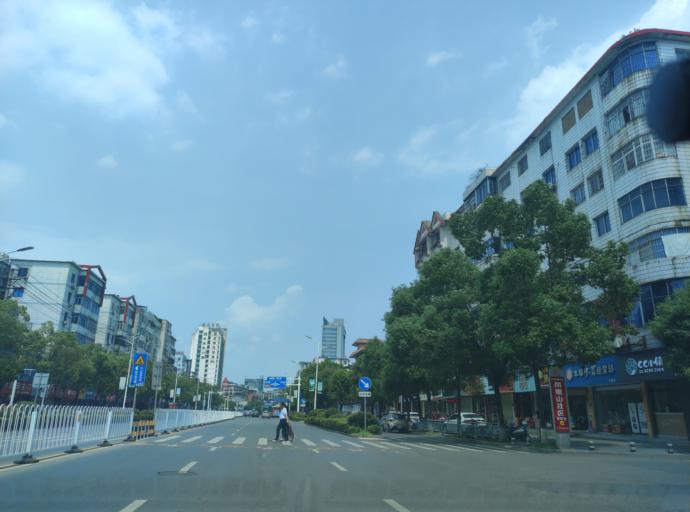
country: CN
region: Jiangxi Sheng
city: Pingxiang
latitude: 27.6396
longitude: 113.8608
